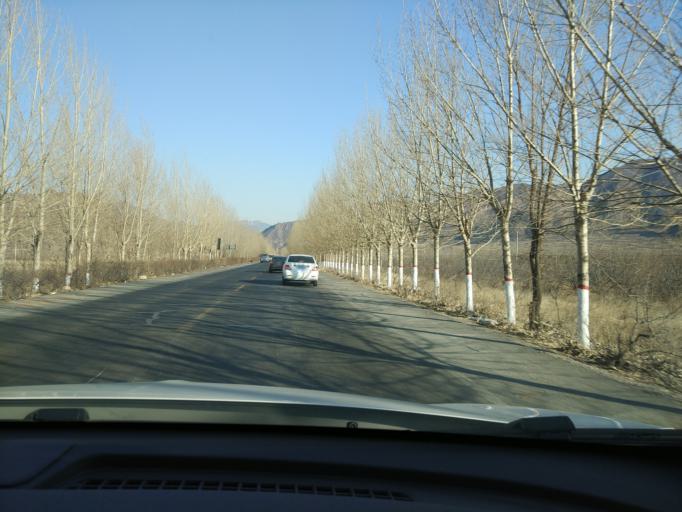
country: CN
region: Hebei
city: Chicheng
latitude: 40.7060
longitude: 115.7861
